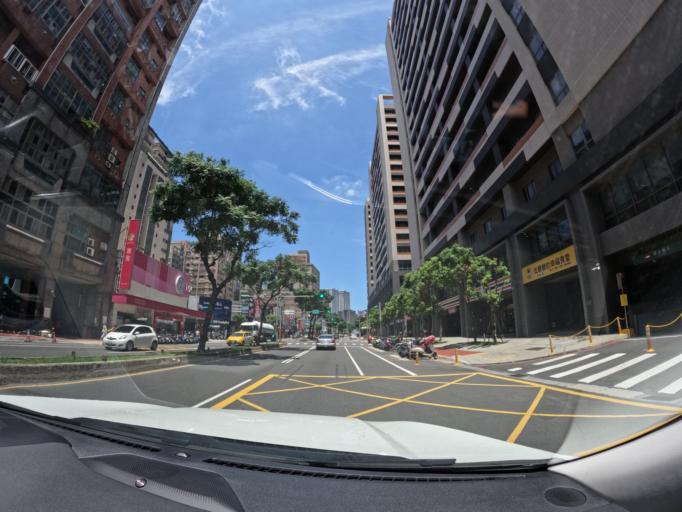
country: TW
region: Taiwan
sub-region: Taoyuan
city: Taoyuan
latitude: 25.0592
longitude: 121.3655
